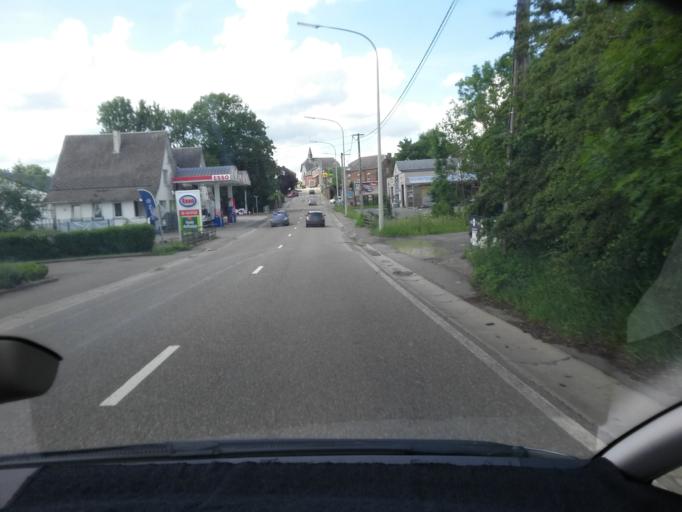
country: BE
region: Wallonia
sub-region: Province de Namur
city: Rochefort
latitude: 50.1652
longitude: 5.2131
